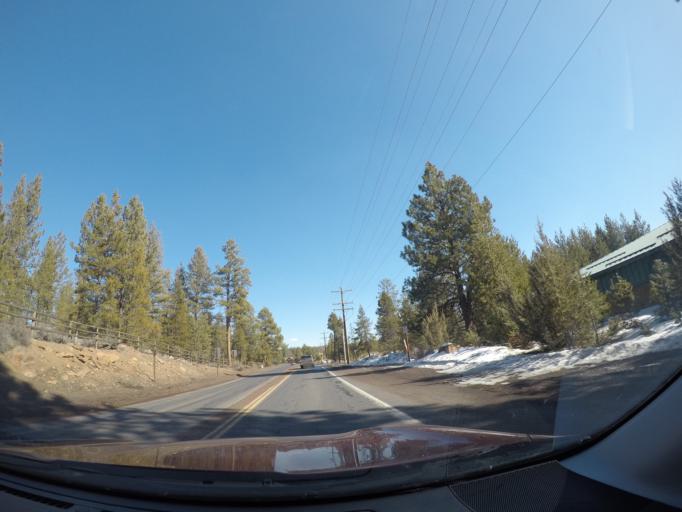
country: US
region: Oregon
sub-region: Deschutes County
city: Sunriver
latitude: 43.8634
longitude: -121.4419
